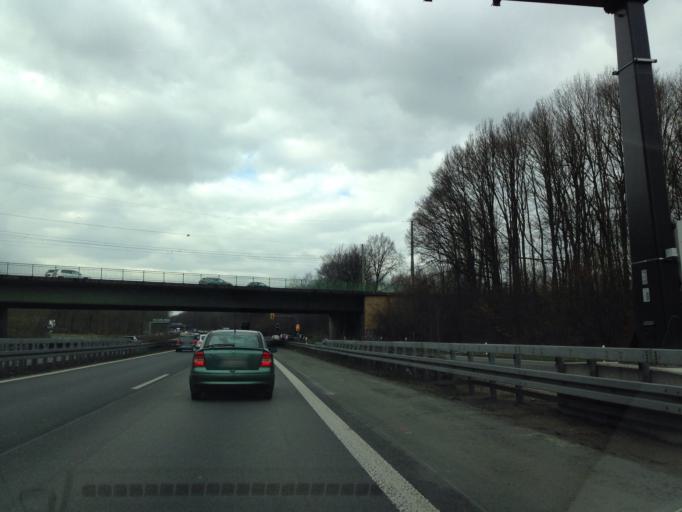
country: DE
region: North Rhine-Westphalia
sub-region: Regierungsbezirk Arnsberg
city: Bochum
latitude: 51.5027
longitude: 7.2605
